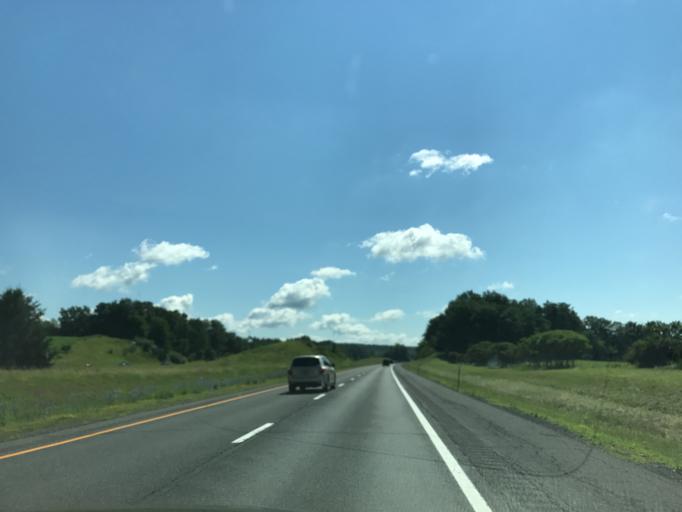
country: US
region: New York
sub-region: Columbia County
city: Niverville
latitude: 42.4832
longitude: -73.6472
